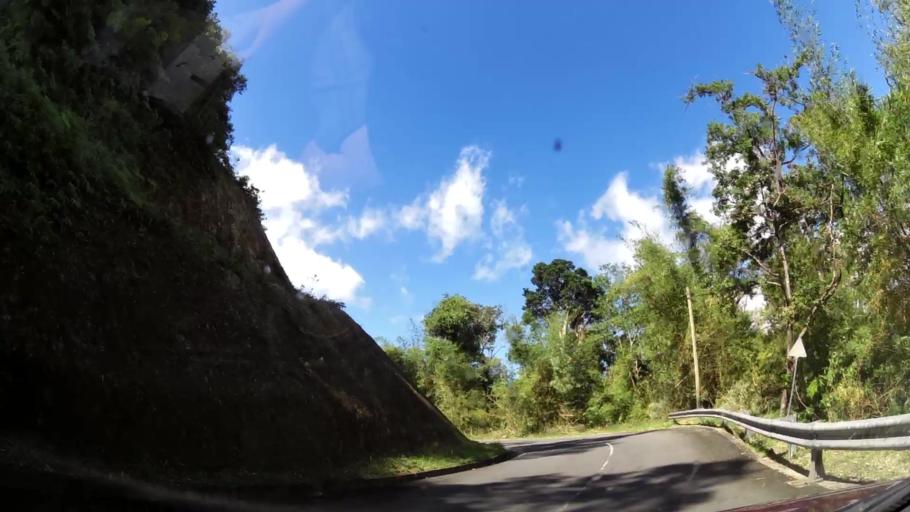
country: DM
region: Saint Paul
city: Pont Casse
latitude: 15.3624
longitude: -61.3550
